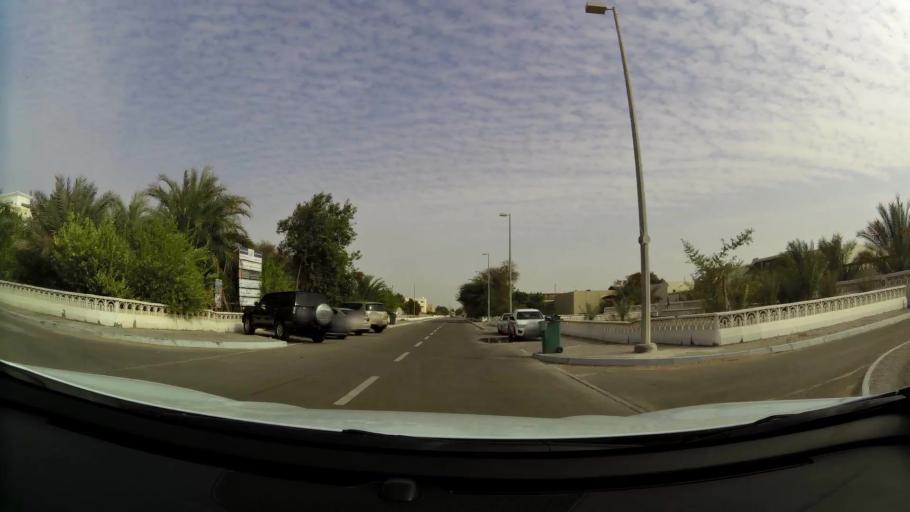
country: AE
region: Abu Dhabi
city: Abu Dhabi
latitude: 24.6096
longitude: 54.7018
